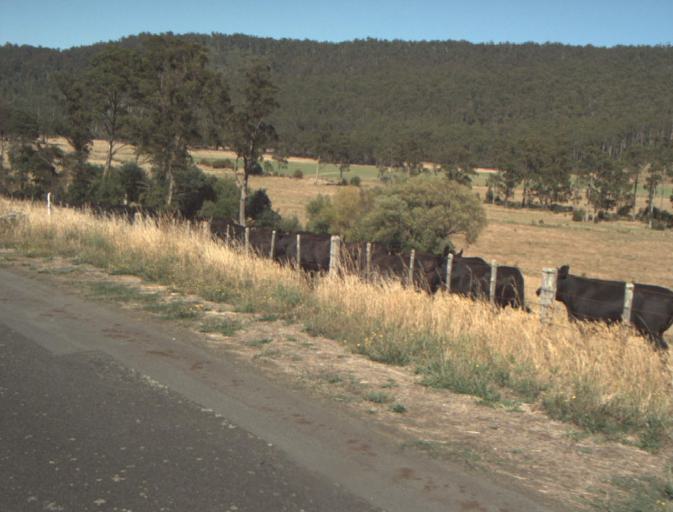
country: AU
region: Tasmania
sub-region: Launceston
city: Newstead
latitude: -41.3459
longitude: 147.3028
